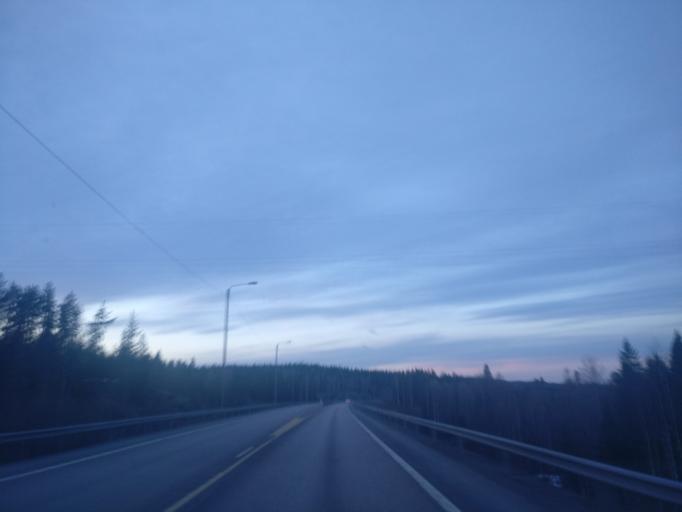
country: FI
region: Central Finland
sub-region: Jyvaeskylae
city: Saeynaetsalo
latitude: 62.2089
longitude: 25.8896
